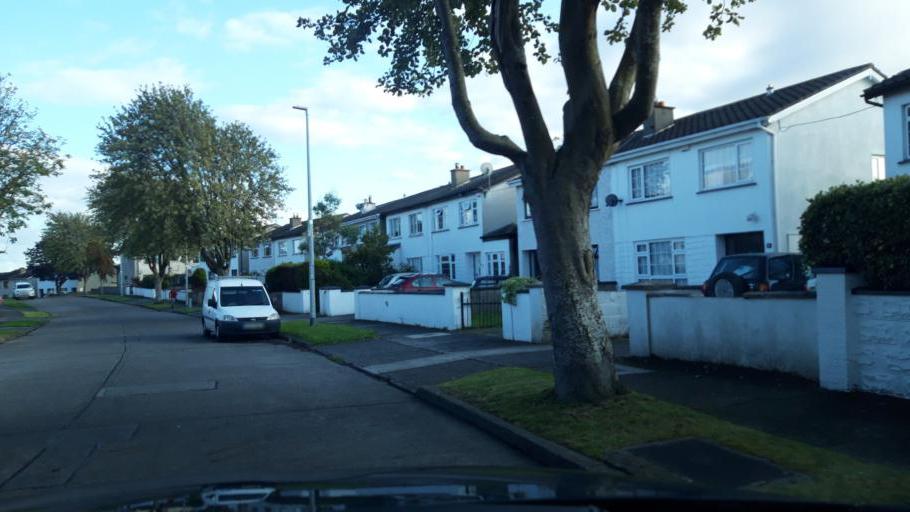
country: IE
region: Leinster
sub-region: Fingal County
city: Blanchardstown
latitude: 53.3986
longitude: -6.3865
